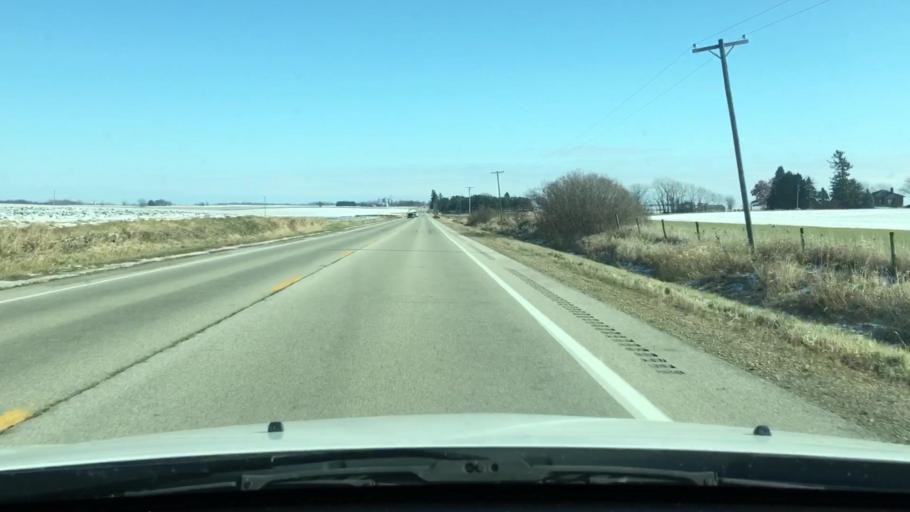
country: US
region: Illinois
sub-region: DeKalb County
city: Malta
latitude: 42.0010
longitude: -88.8625
